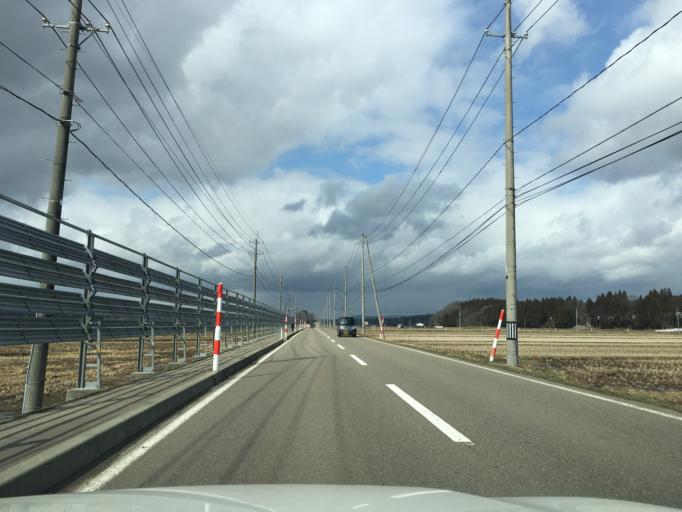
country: JP
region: Akita
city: Takanosu
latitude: 40.1280
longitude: 140.3633
